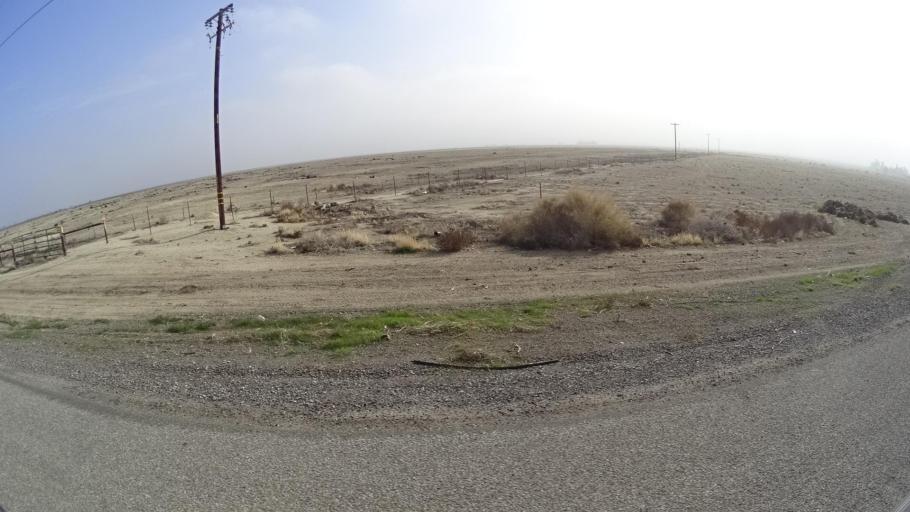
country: US
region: California
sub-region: Kern County
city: Ford City
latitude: 35.2128
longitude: -119.4005
